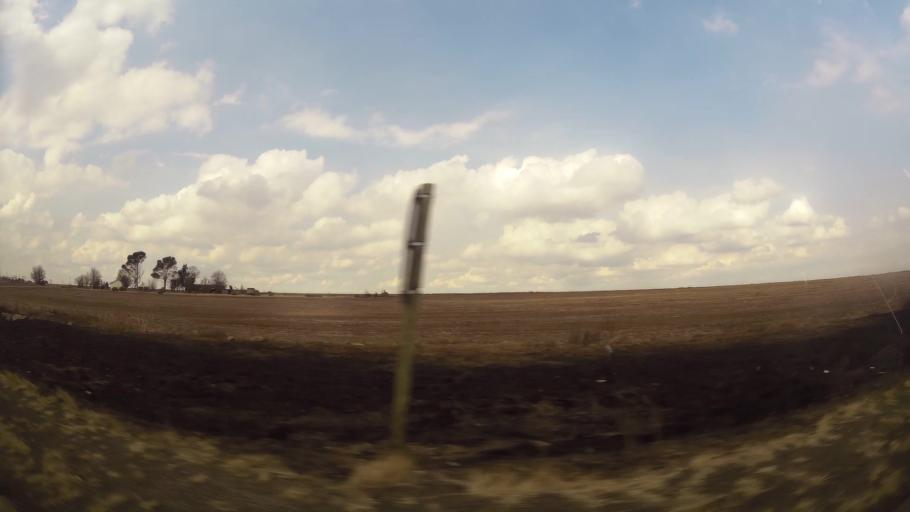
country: ZA
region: Orange Free State
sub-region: Fezile Dabi District Municipality
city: Sasolburg
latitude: -26.8311
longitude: 27.8986
